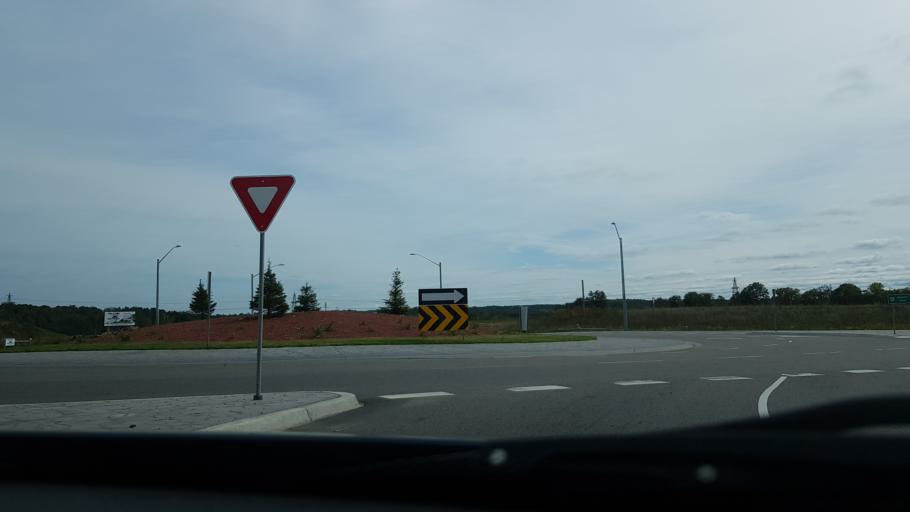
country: CA
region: Ontario
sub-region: Wellington County
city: Guelph
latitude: 43.4722
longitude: -80.3061
